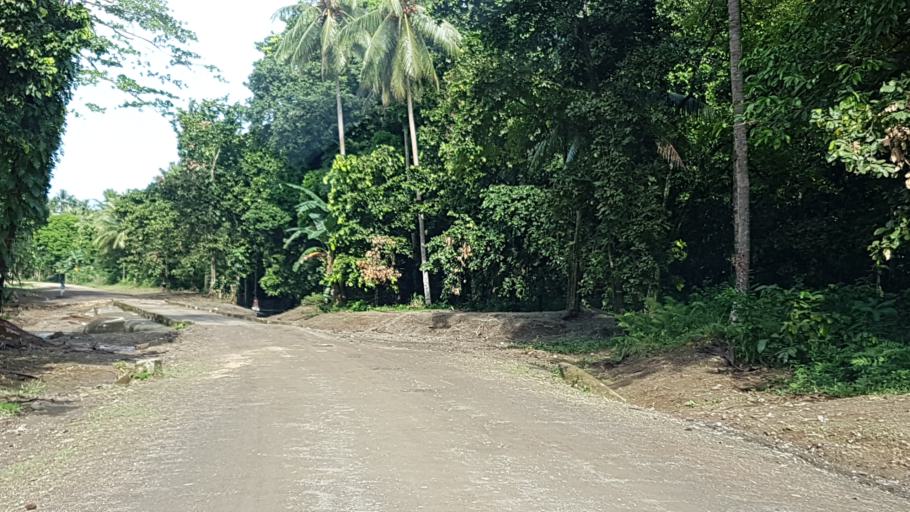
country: PG
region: Milne Bay
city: Alotau
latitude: -10.3031
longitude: 150.7272
